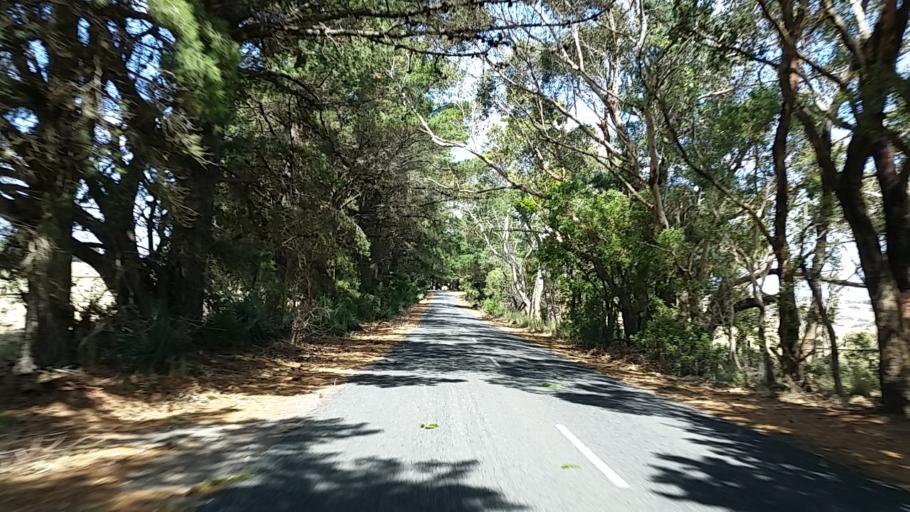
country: AU
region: South Australia
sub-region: Alexandrina
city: Mount Compass
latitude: -35.4382
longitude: 138.6089
